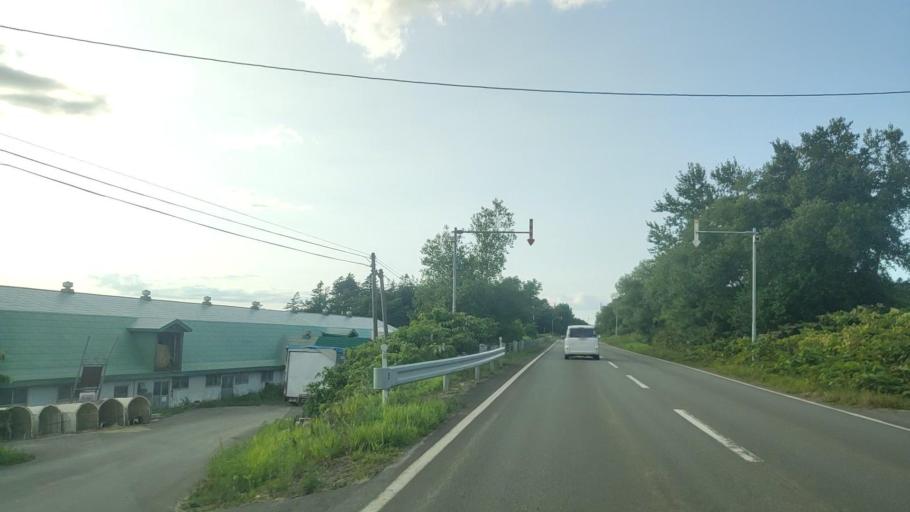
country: JP
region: Hokkaido
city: Makubetsu
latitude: 45.0452
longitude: 141.7537
